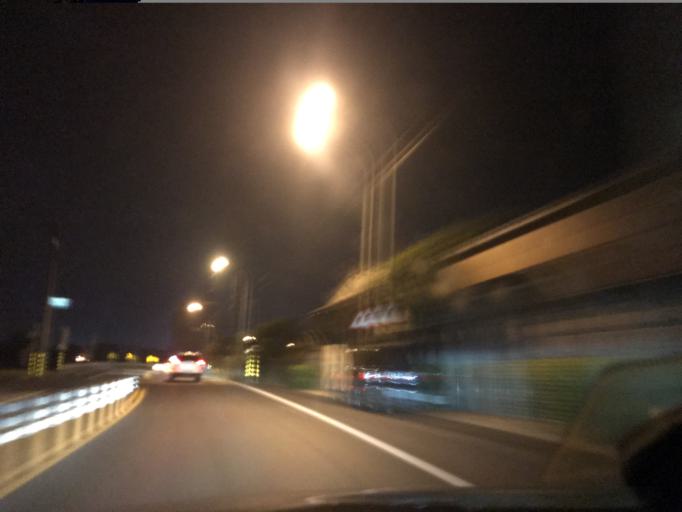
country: TW
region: Taiwan
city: Daxi
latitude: 24.8795
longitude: 121.2191
